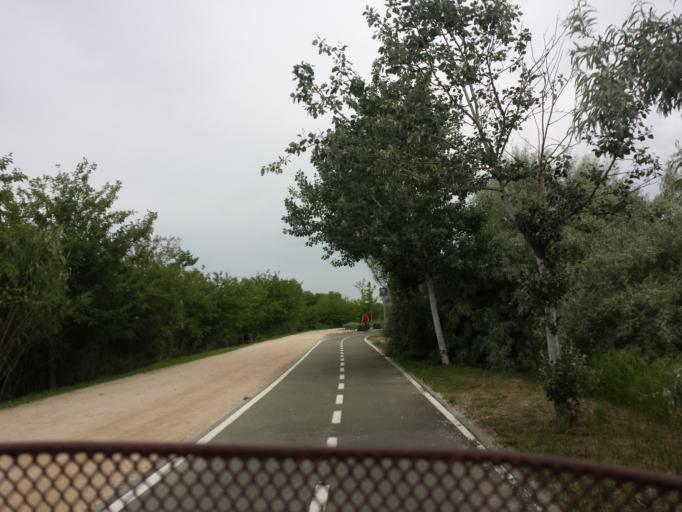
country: ES
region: Aragon
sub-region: Provincia de Zaragoza
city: Almozara
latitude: 41.6754
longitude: -0.9069
